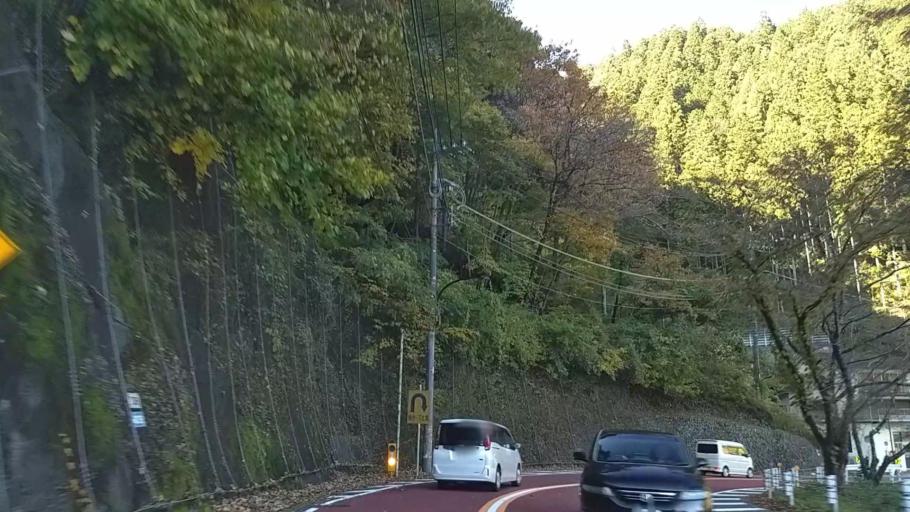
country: JP
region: Yamanashi
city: Uenohara
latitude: 35.7862
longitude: 139.0427
